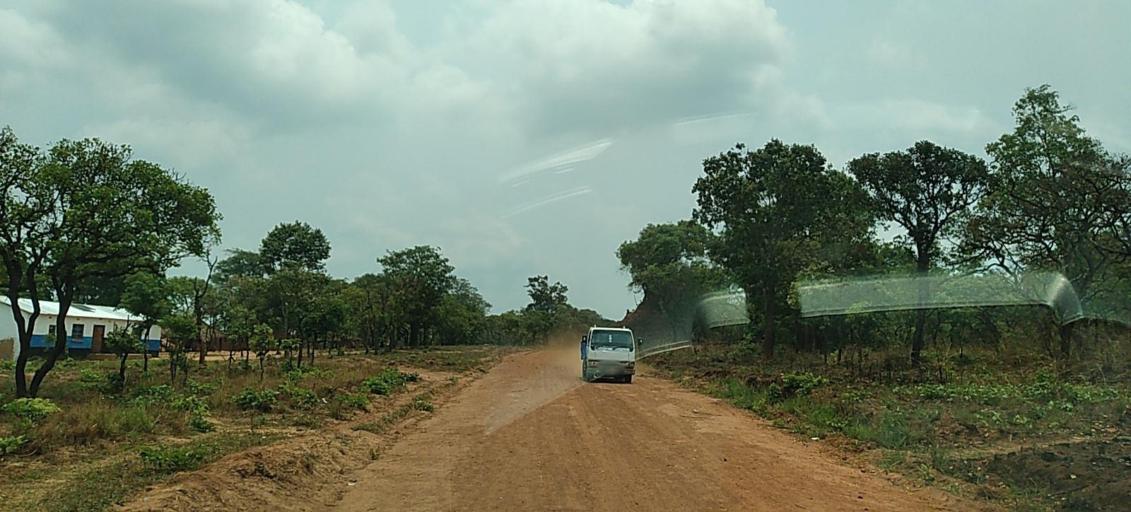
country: ZM
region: North-Western
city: Mwinilunga
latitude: -11.4557
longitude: 24.7582
